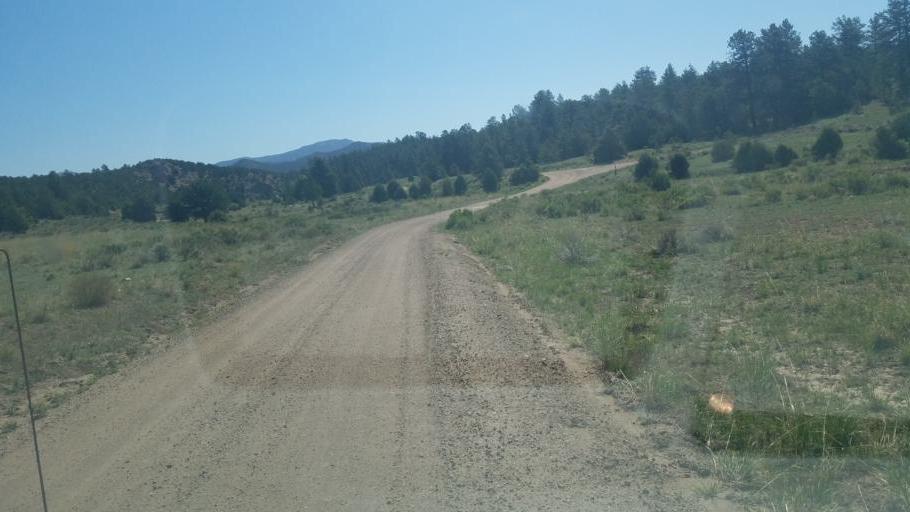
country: US
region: Colorado
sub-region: Custer County
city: Westcliffe
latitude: 38.2872
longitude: -105.4510
